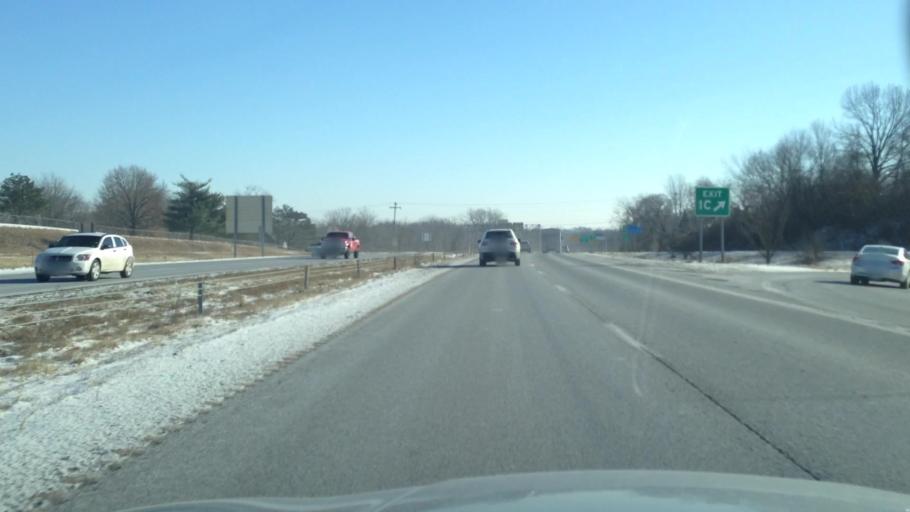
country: US
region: Missouri
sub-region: Clay County
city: Gladstone
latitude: 39.1795
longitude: -94.5751
